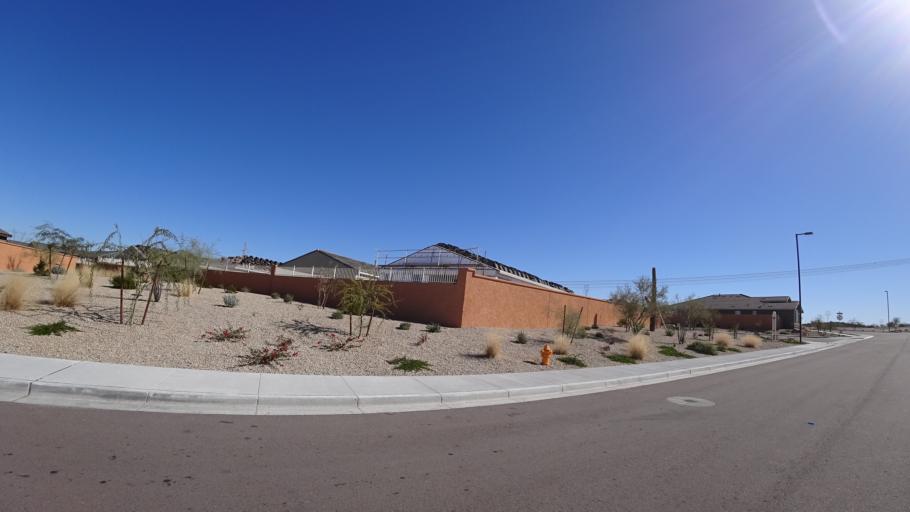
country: US
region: Arizona
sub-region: Maricopa County
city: Goodyear
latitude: 33.3460
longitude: -112.4260
